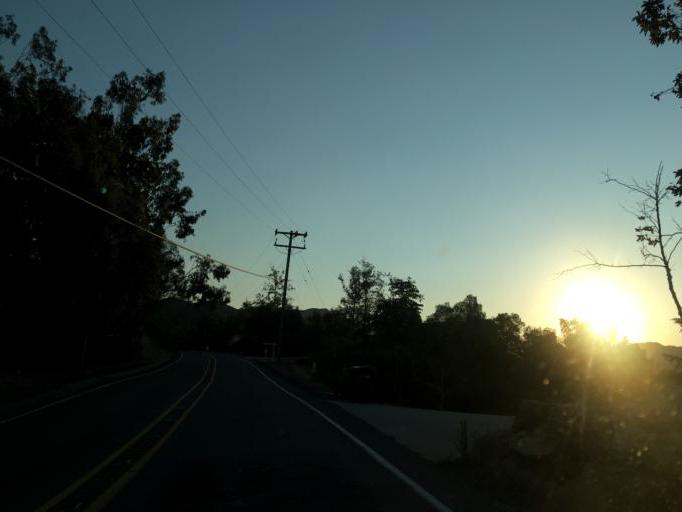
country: US
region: California
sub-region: Los Angeles County
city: Malibu Beach
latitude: 34.0966
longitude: -118.6752
